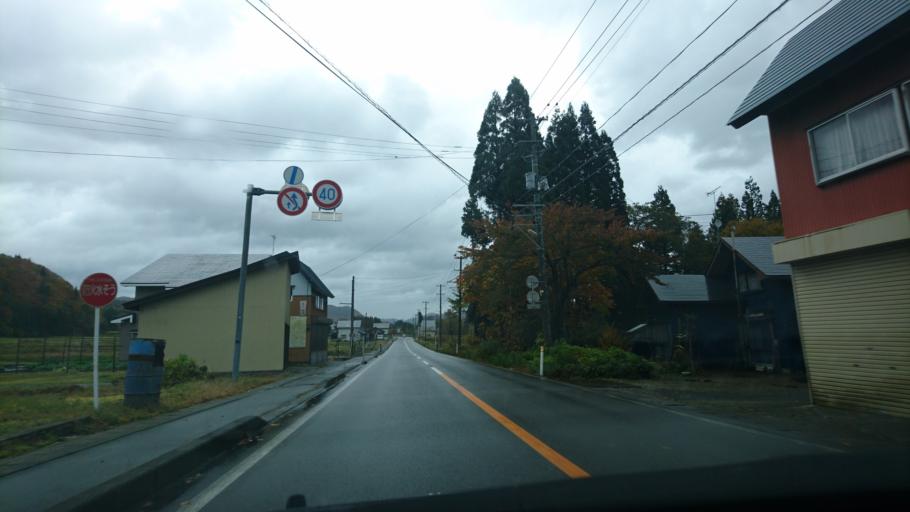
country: JP
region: Akita
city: Kakunodatemachi
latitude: 39.4546
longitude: 140.7689
